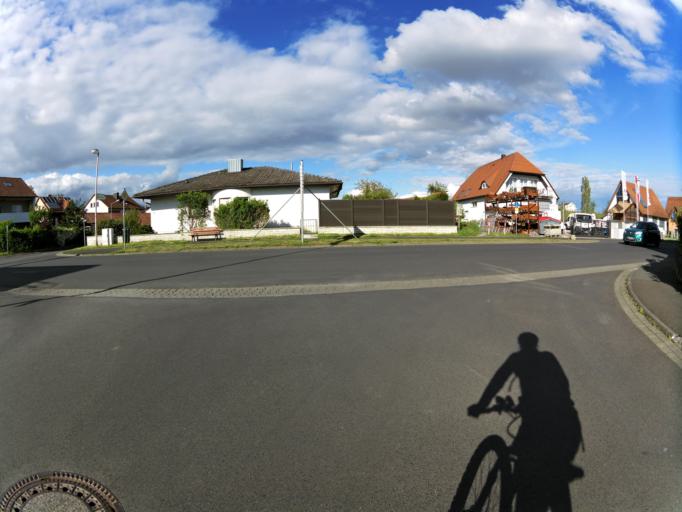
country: DE
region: Bavaria
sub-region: Regierungsbezirk Unterfranken
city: Volkach
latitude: 49.8592
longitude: 10.2324
